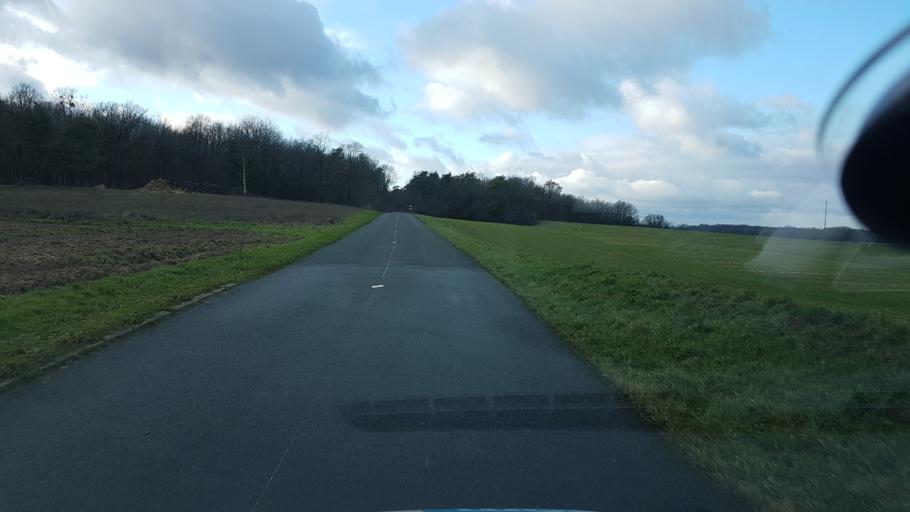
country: FR
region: Ile-de-France
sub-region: Departement de Seine-et-Marne
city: Montigny-sur-Loing
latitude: 48.2757
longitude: 2.7877
